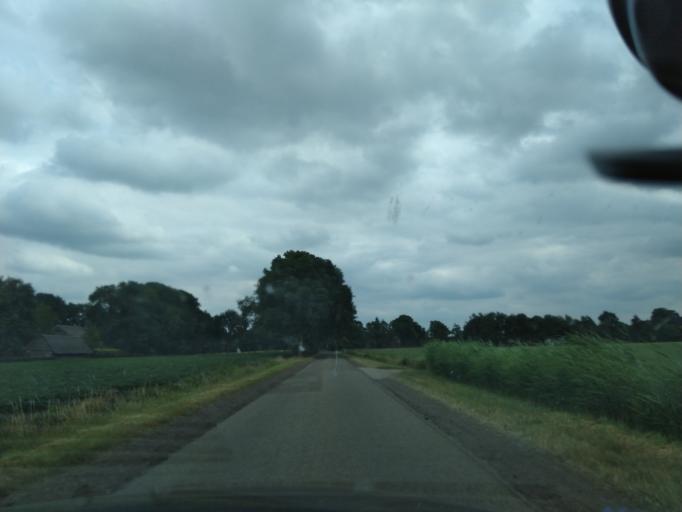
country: NL
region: Groningen
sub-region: Gemeente Vlagtwedde
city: Vlagtwedde
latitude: 53.0776
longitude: 7.1150
